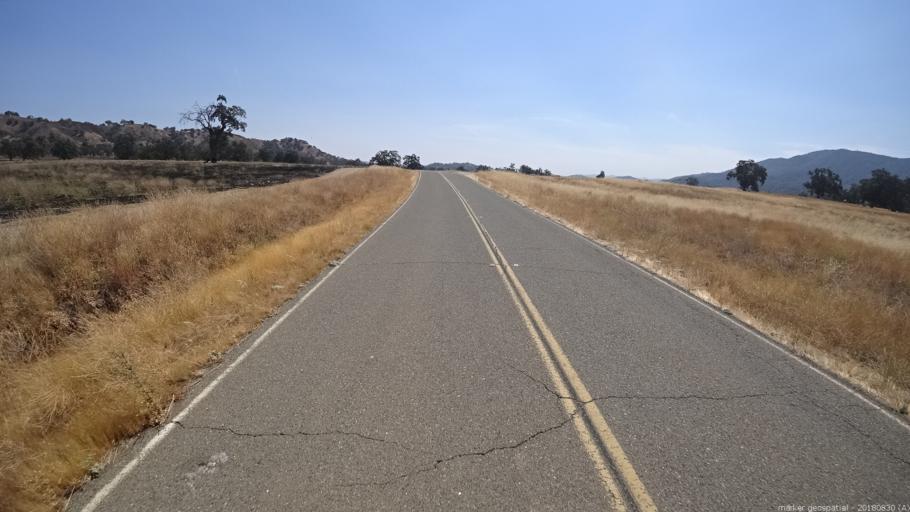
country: US
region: California
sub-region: Monterey County
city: King City
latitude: 35.9701
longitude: -121.3162
